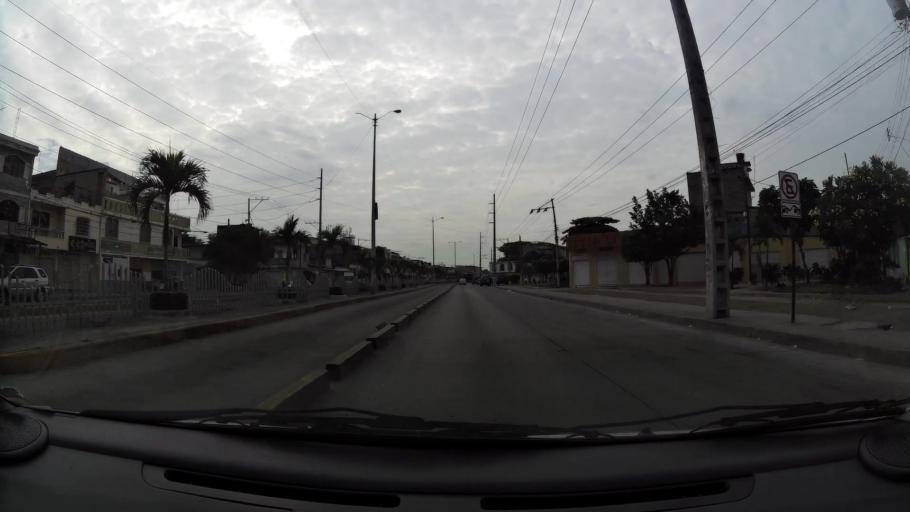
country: EC
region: Guayas
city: Guayaquil
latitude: -2.2510
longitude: -79.8879
